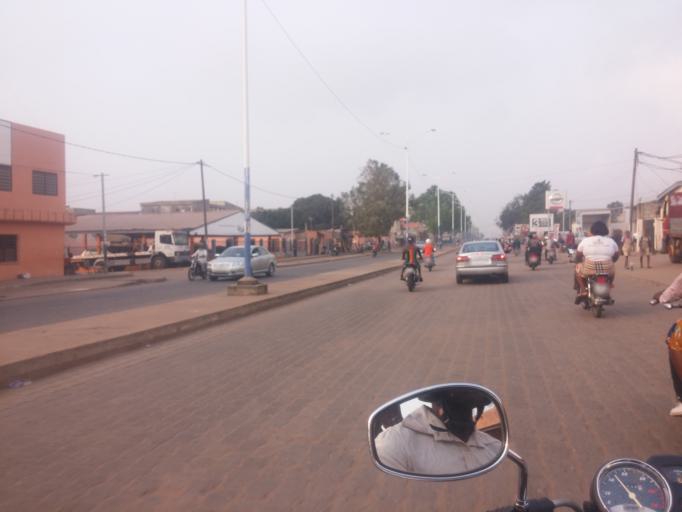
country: TG
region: Maritime
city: Lome
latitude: 6.1566
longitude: 1.2516
